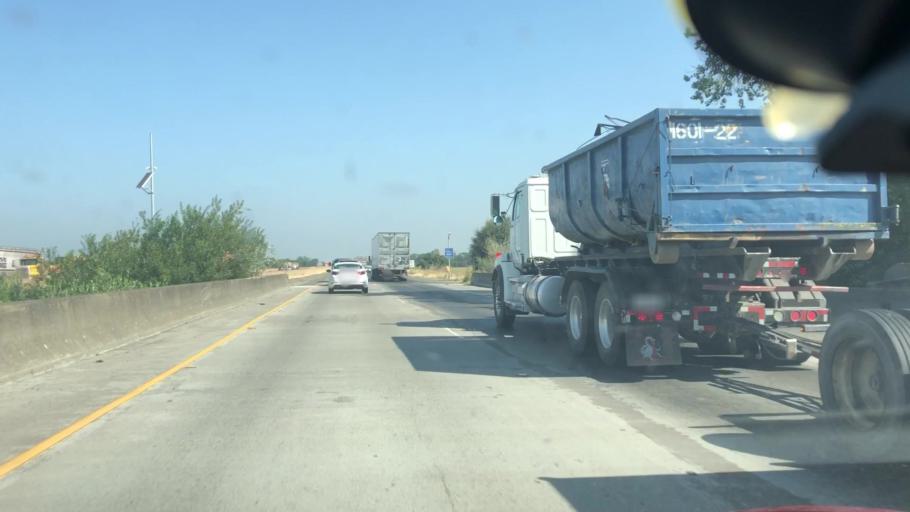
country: US
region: California
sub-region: San Joaquin County
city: Thornton
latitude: 38.2572
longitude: -121.4487
